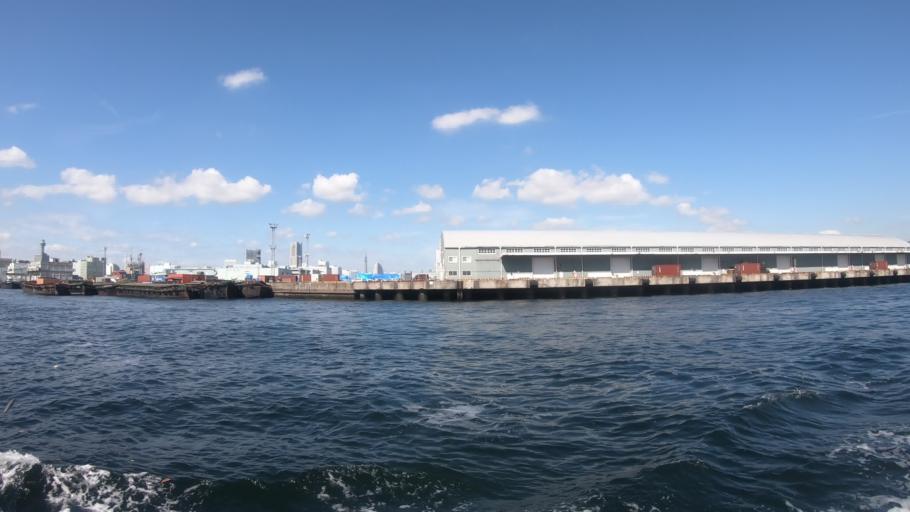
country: JP
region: Kanagawa
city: Yokohama
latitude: 35.4464
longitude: 139.6644
